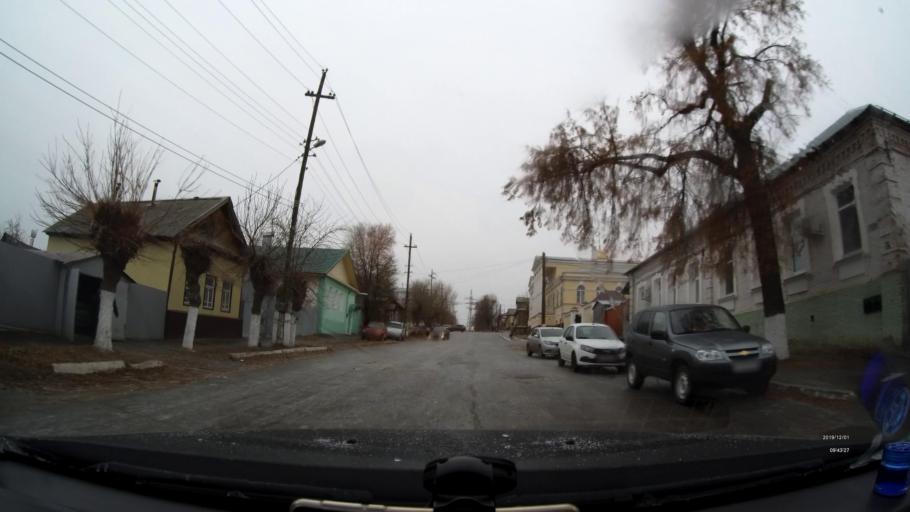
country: RU
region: Saratov
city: Vol'sk
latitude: 52.0433
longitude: 47.3822
